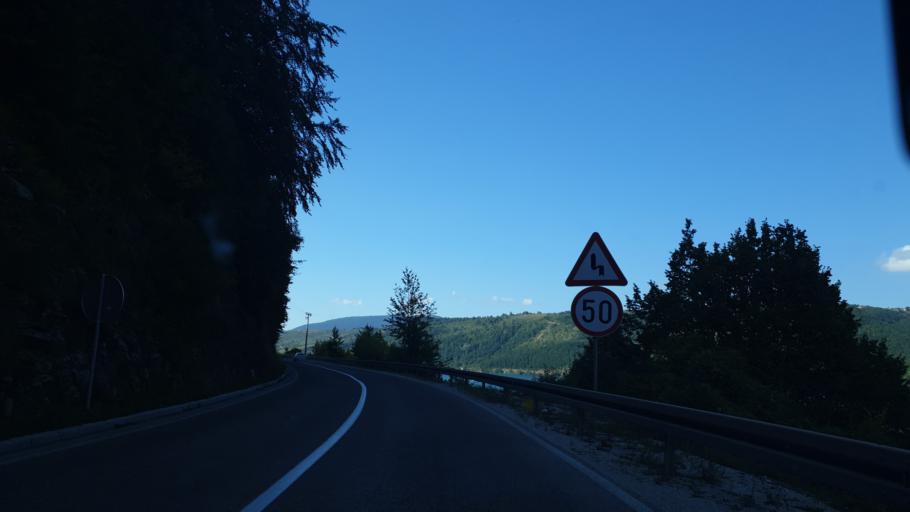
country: RS
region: Central Serbia
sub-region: Zlatiborski Okrug
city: Nova Varos
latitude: 43.5026
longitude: 19.8210
